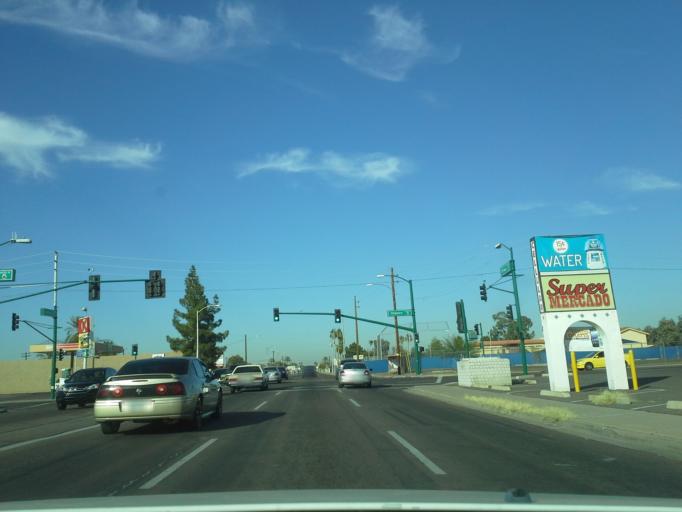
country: US
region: Arizona
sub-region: Maricopa County
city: Phoenix
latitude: 33.4873
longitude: -112.0999
